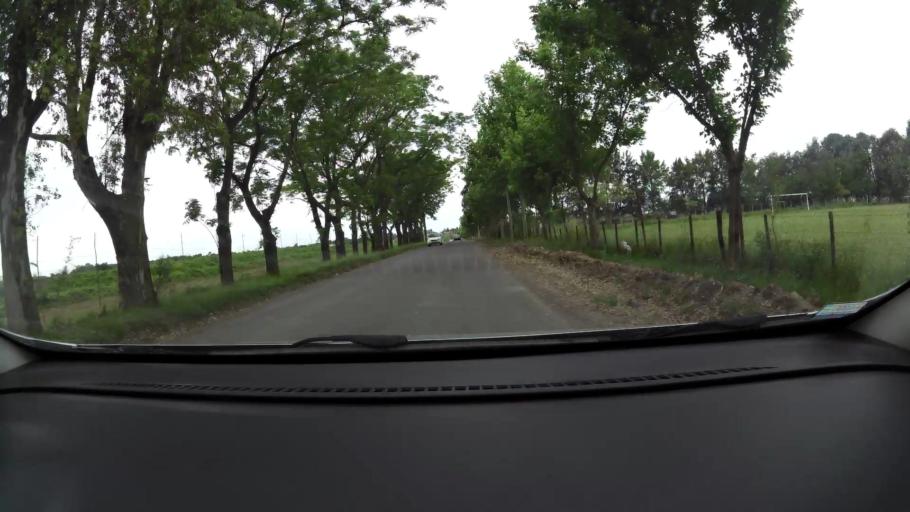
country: AR
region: Buenos Aires
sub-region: Partido de Campana
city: Campana
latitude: -34.2014
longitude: -58.9486
